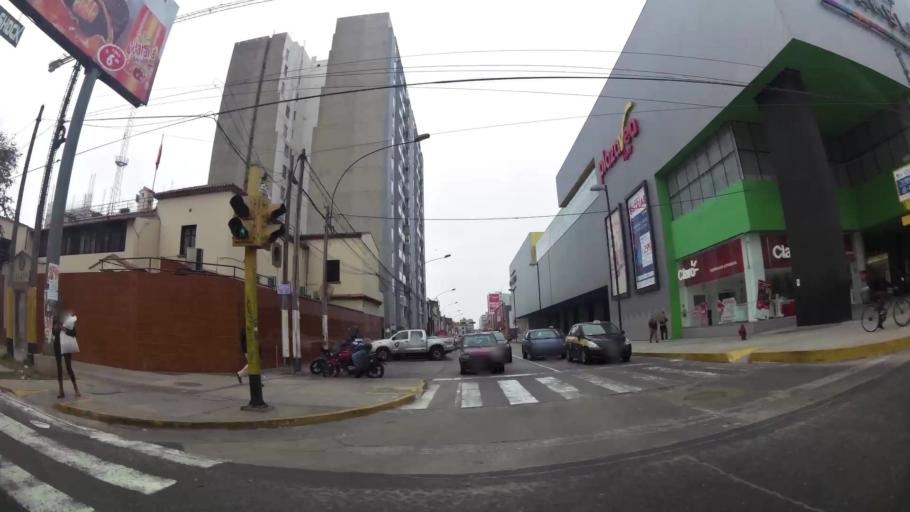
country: PE
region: Lima
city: Lima
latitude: -12.0671
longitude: -77.0476
